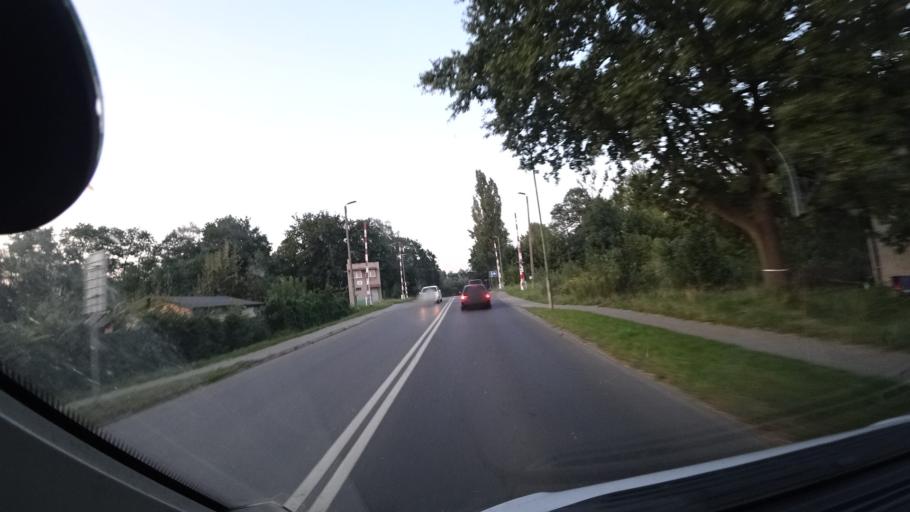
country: PL
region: Silesian Voivodeship
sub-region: Zabrze
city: Zabrze
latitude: 50.3428
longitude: 18.7789
